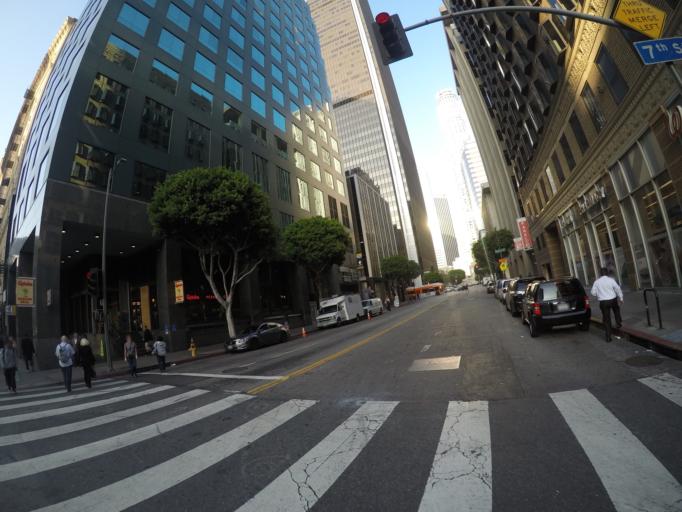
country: US
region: California
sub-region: Los Angeles County
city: Los Angeles
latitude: 34.0481
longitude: -118.2576
